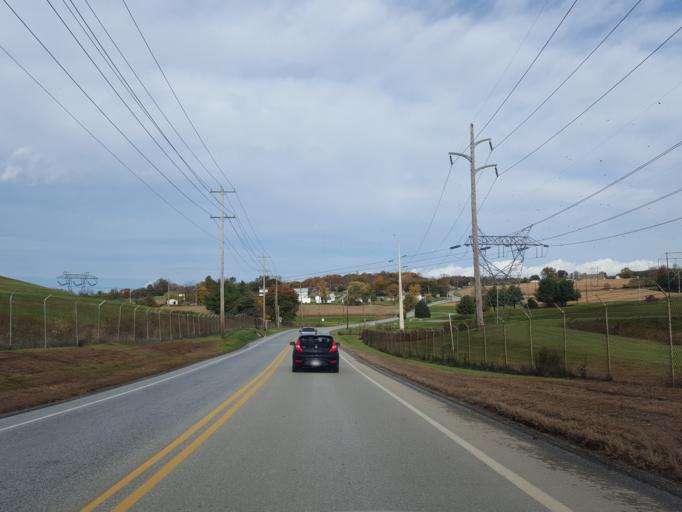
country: US
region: Pennsylvania
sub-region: York County
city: Hallam
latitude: 39.9630
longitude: -76.5898
